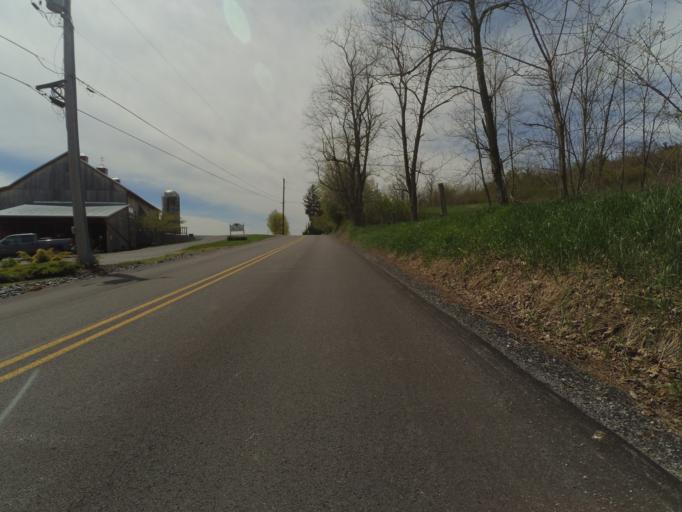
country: US
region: Pennsylvania
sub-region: Blair County
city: Tyrone
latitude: 40.7209
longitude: -78.1255
